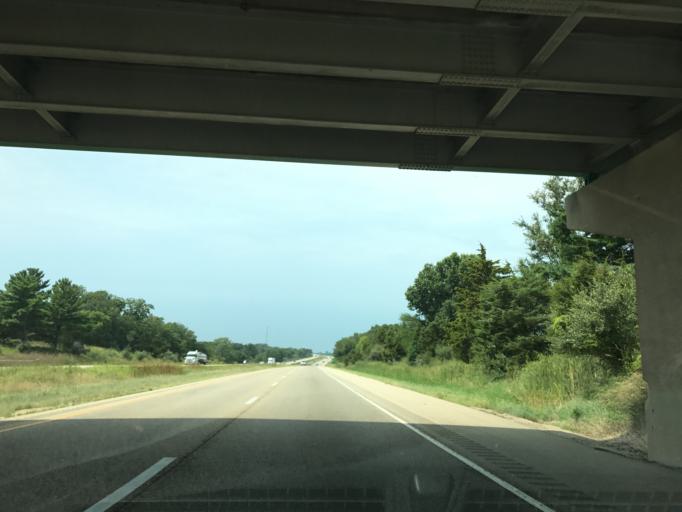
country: US
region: Illinois
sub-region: Bureau County
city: Depue
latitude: 41.3998
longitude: -89.3539
